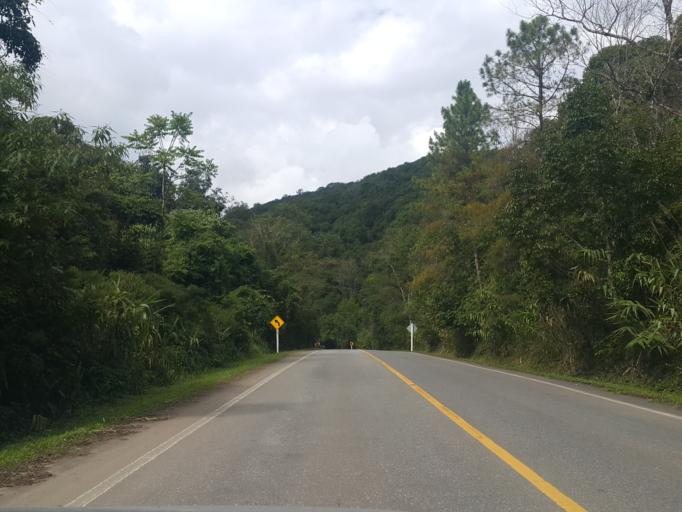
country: TH
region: Chiang Mai
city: Mae Chaem
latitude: 18.5153
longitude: 98.5044
